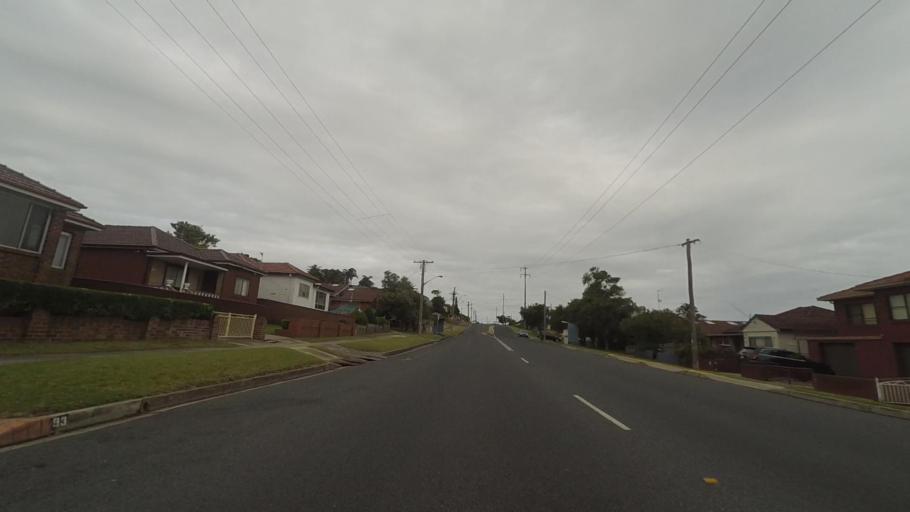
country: AU
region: New South Wales
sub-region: Wollongong
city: Port Kembla
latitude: -34.4877
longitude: 150.8975
